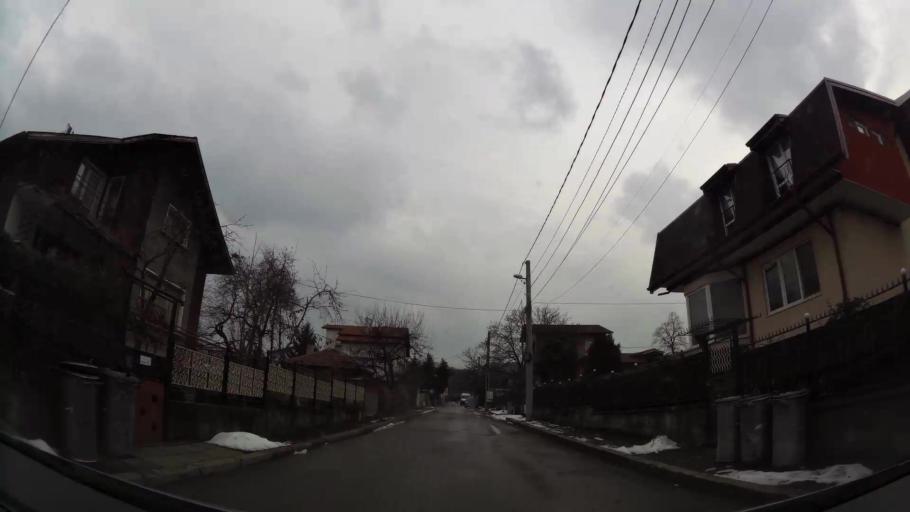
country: BG
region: Sofiya
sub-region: Obshtina Bozhurishte
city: Bozhurishte
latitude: 42.6981
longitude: 23.2232
